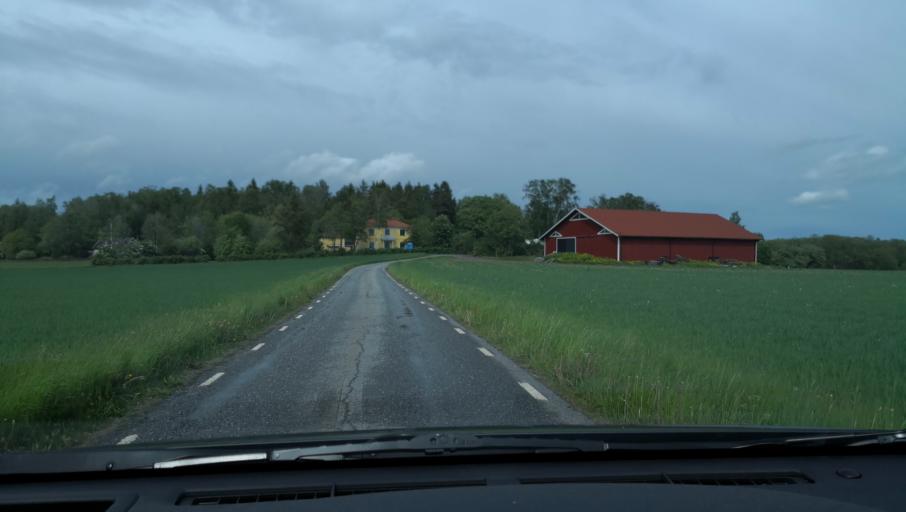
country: SE
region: Uppsala
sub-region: Enkopings Kommun
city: Orsundsbro
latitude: 59.7188
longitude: 17.4256
